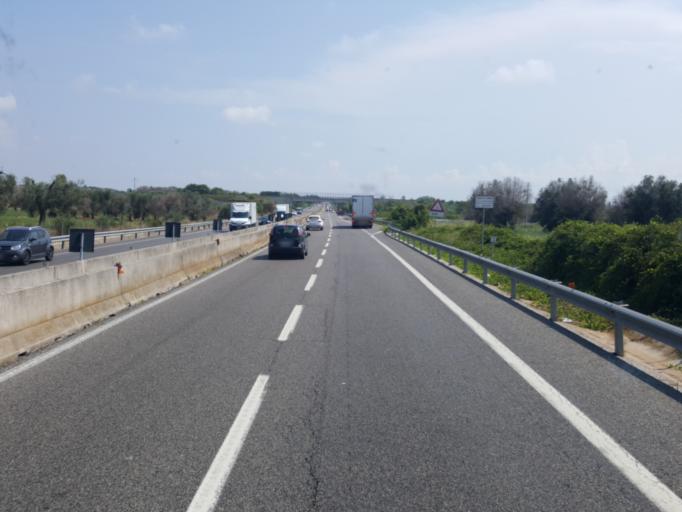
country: IT
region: Apulia
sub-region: Provincia di Brindisi
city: Torchiarolo
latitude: 40.4900
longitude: 18.0385
